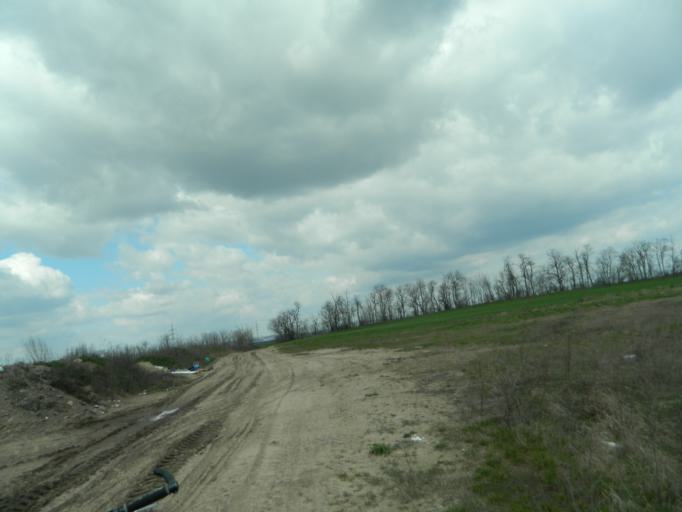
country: HU
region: Fejer
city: Szabadbattyan
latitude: 47.1392
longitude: 18.3735
